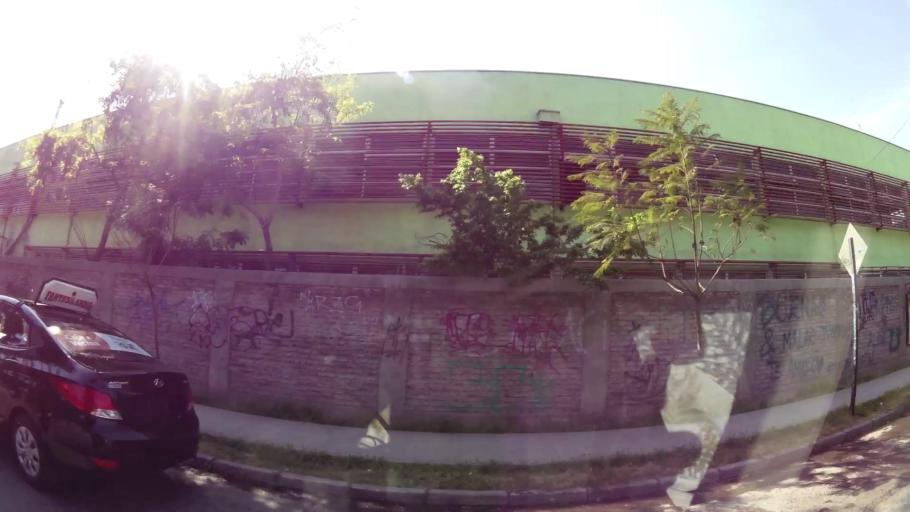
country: CL
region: Santiago Metropolitan
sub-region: Provincia de Santiago
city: La Pintana
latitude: -33.5628
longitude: -70.6648
